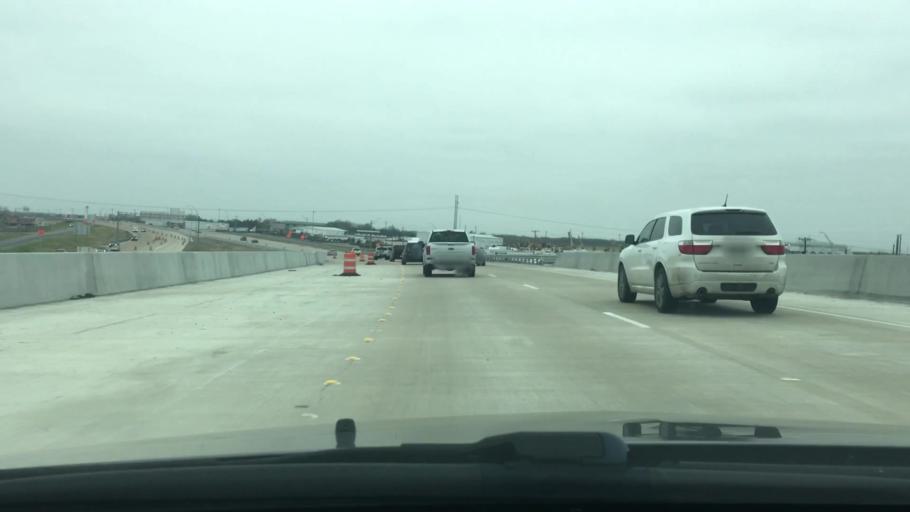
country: US
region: Texas
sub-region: Navarro County
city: Corsicana
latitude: 32.0655
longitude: -96.4522
